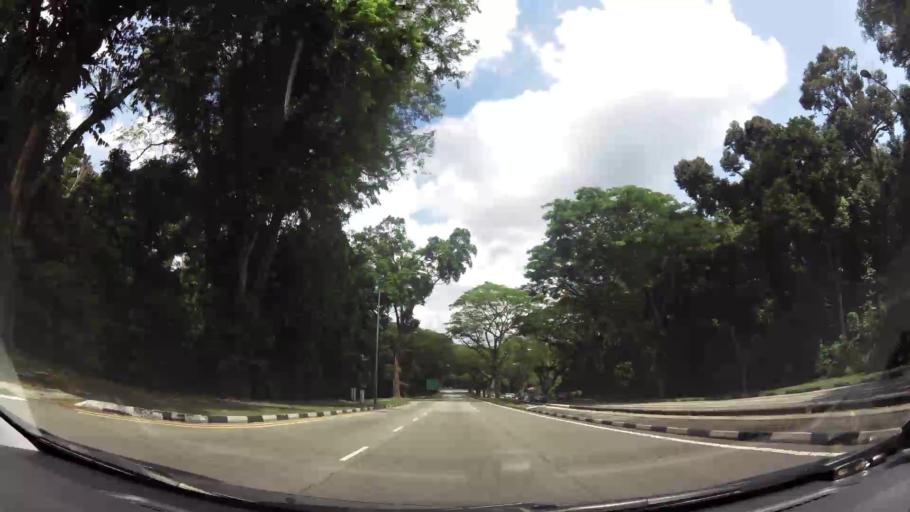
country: MY
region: Johor
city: Johor Bahru
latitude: 1.3909
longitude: 103.8181
